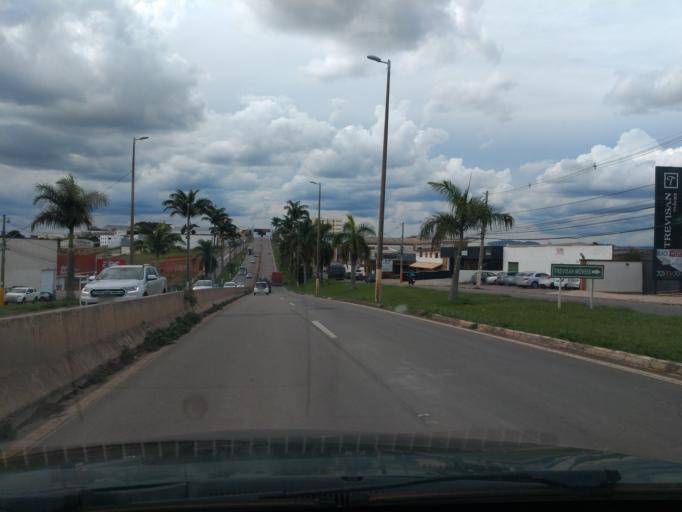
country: BR
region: Minas Gerais
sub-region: Varginha
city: Varginha
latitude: -21.5879
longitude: -45.4378
